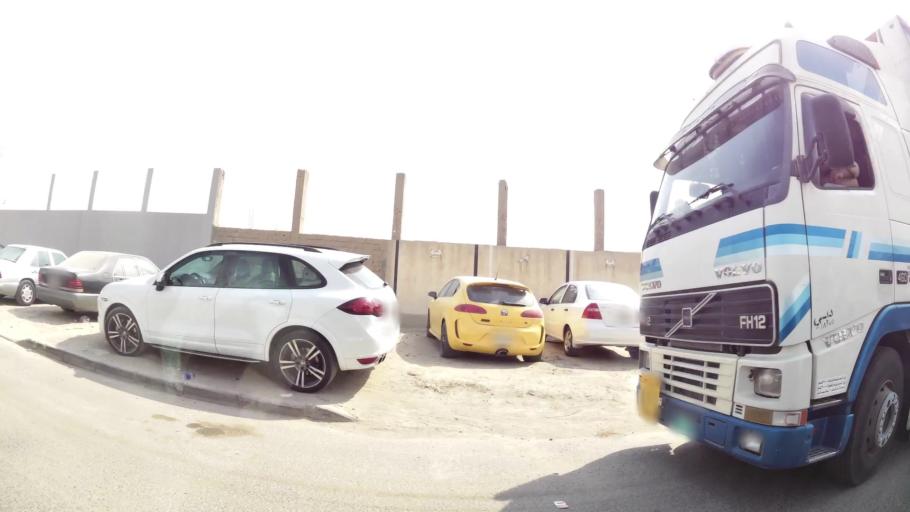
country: KW
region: Al Asimah
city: Ash Shamiyah
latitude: 29.3308
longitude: 47.9386
